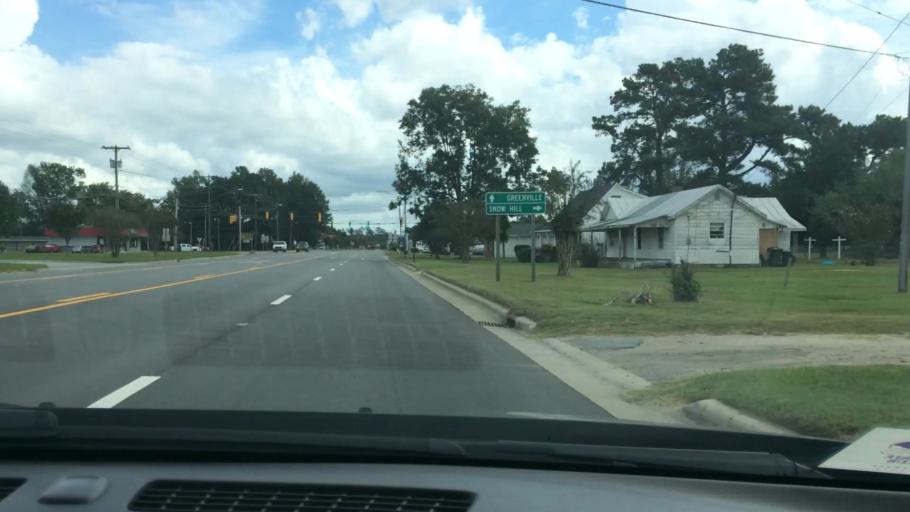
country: US
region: North Carolina
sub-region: Pitt County
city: Farmville
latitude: 35.5822
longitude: -77.5950
